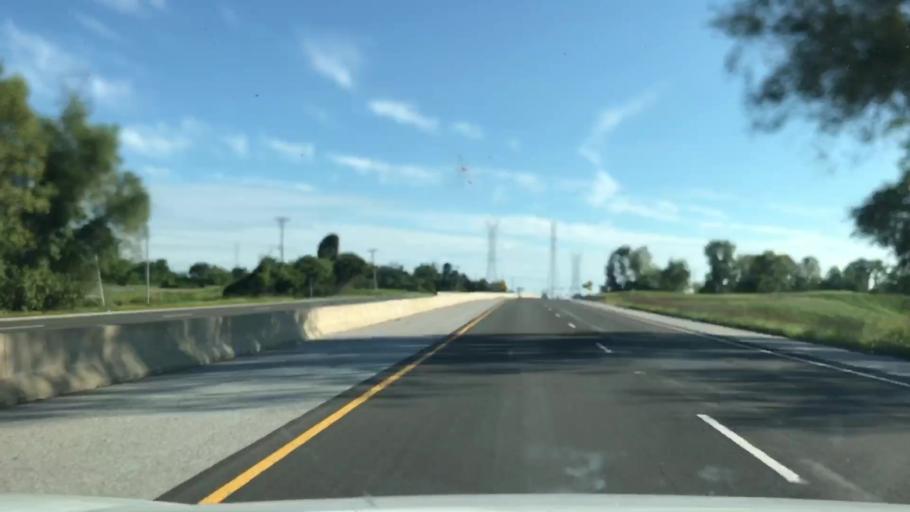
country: US
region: Illinois
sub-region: Madison County
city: Hartford
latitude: 38.8077
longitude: -90.0989
